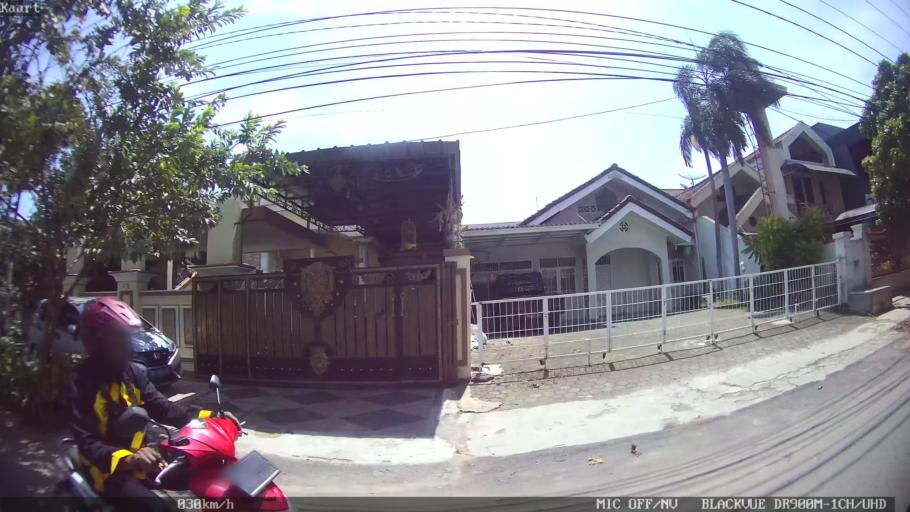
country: ID
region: Lampung
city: Kedaton
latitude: -5.3887
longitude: 105.2816
